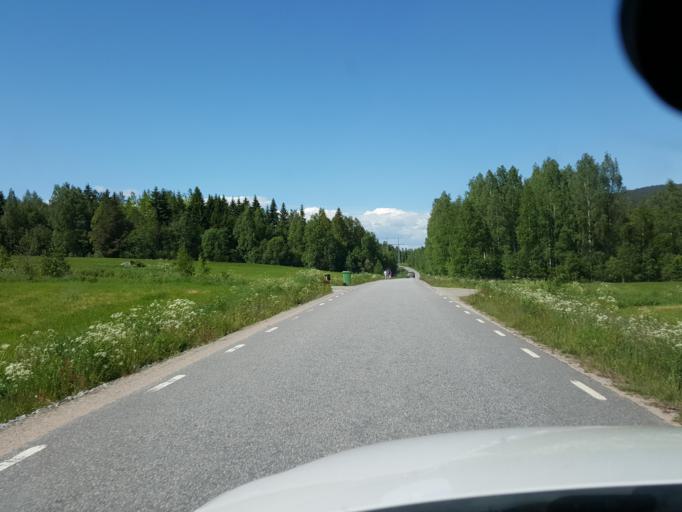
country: SE
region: Gaevleborg
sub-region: Ljusdals Kommun
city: Jaervsoe
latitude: 61.7253
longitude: 16.2873
